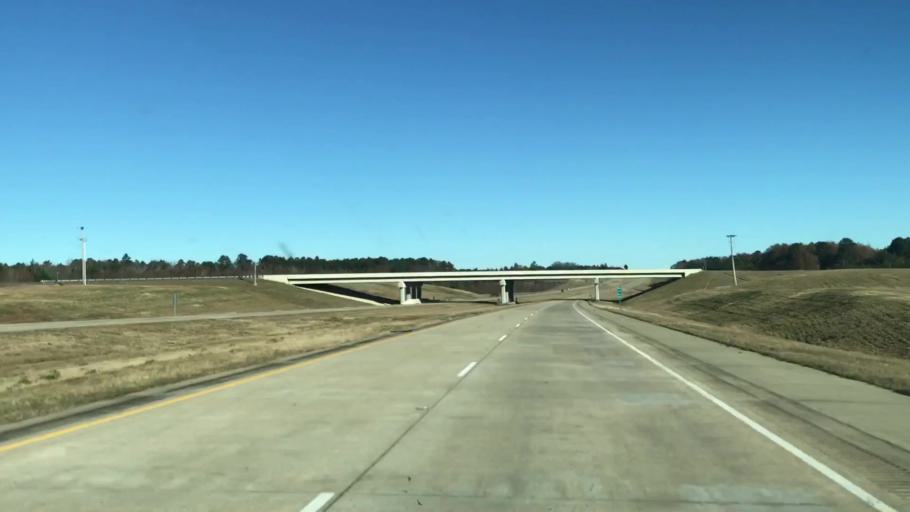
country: US
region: Louisiana
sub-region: Caddo Parish
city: Vivian
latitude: 32.9952
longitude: -93.9096
